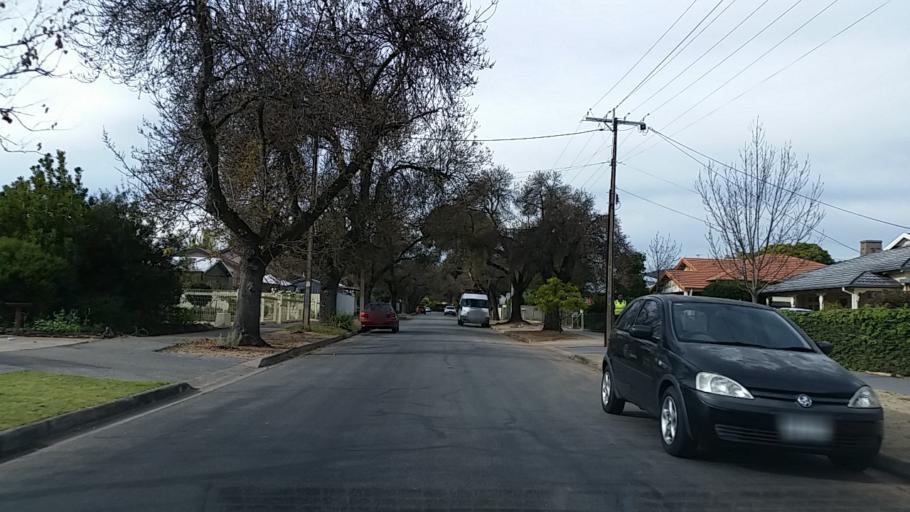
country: AU
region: South Australia
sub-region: Mitcham
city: Clarence Gardens
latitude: -34.9843
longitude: 138.5879
